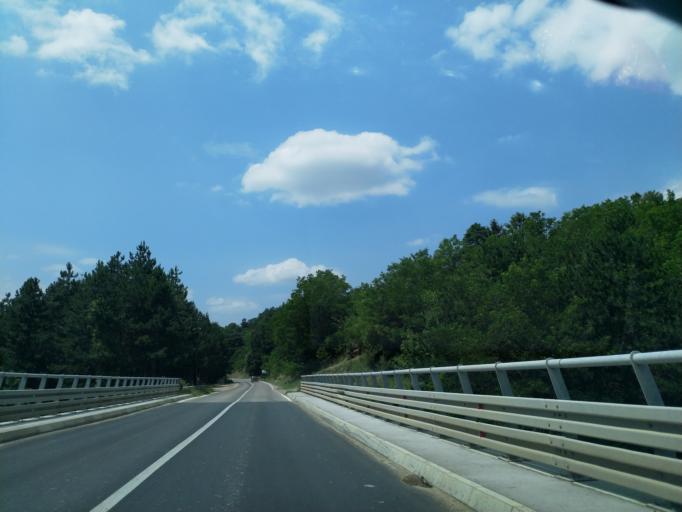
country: RS
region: Central Serbia
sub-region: Rasinski Okrug
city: Aleksandrovac
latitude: 43.4153
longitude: 21.1829
